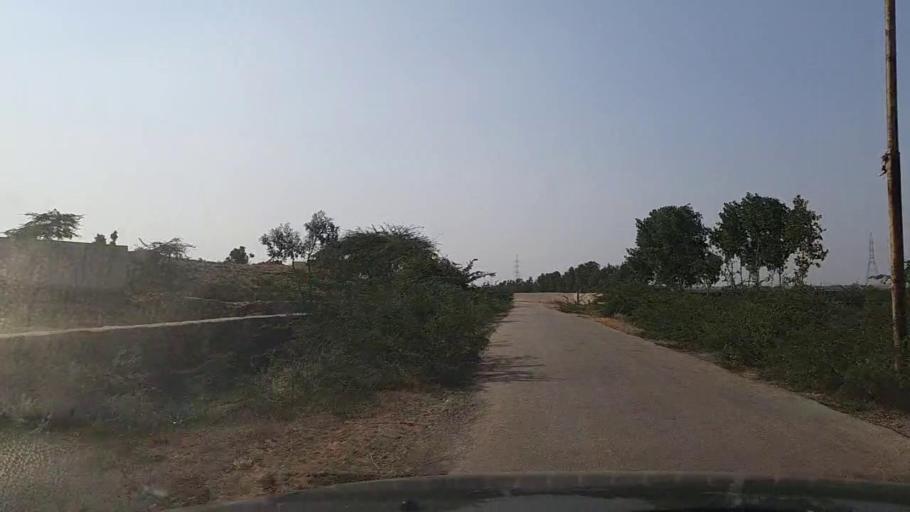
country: PK
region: Sindh
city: Gharo
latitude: 24.7716
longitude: 67.5592
